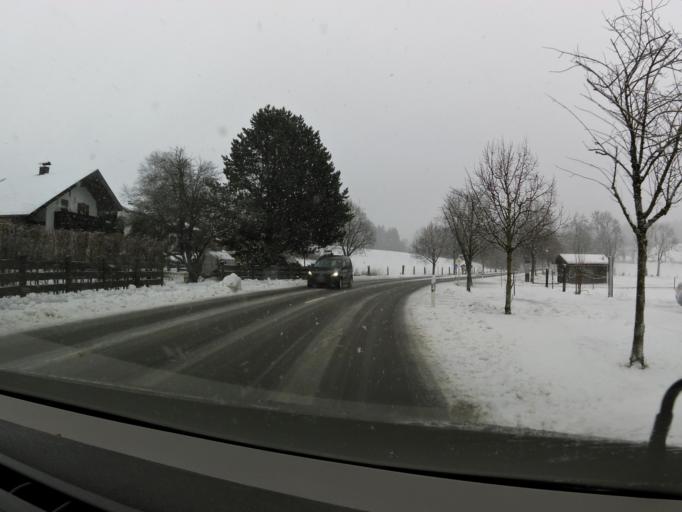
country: DE
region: Bavaria
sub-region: Upper Bavaria
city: Waakirchen
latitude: 47.7636
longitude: 11.6929
